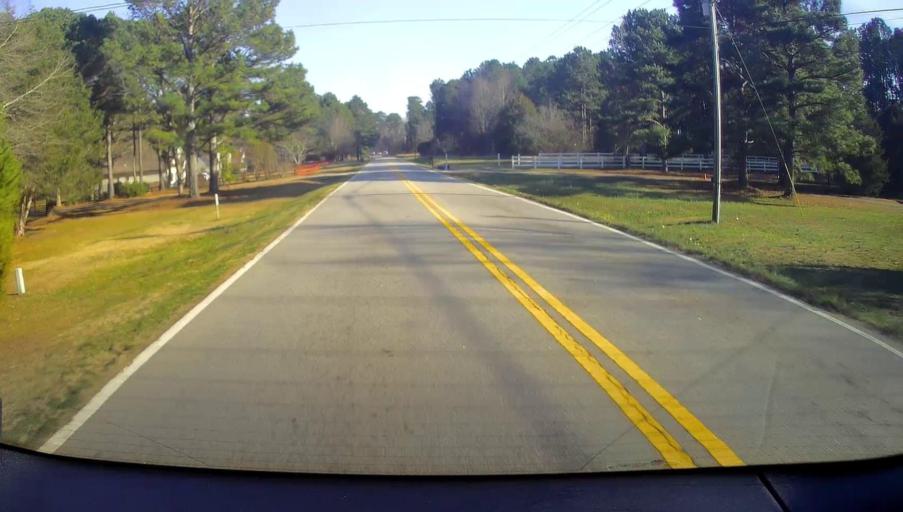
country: US
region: Georgia
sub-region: Henry County
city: Locust Grove
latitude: 33.3546
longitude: -84.1555
